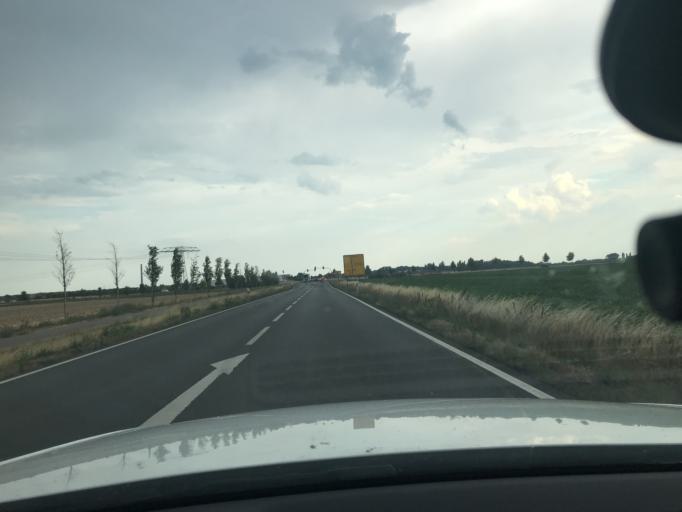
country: DE
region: Saxony
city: Markranstadt
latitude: 51.3184
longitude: 12.2106
